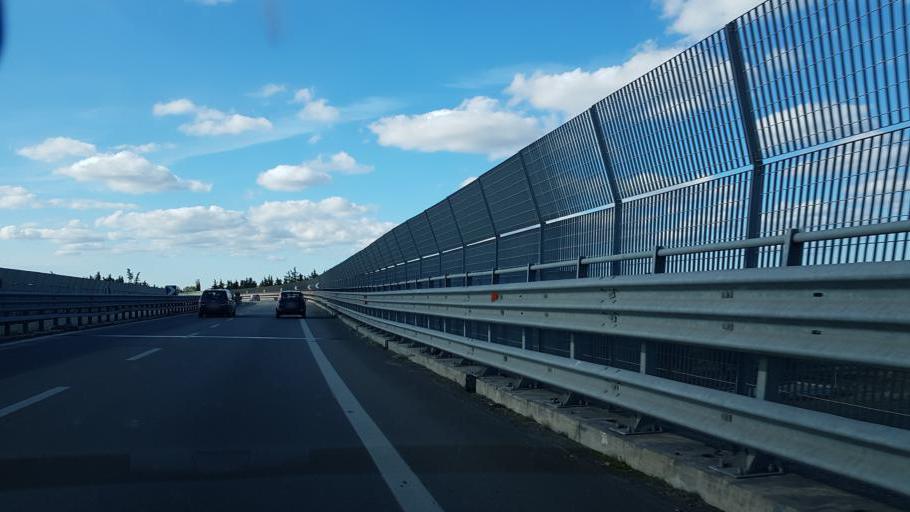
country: IT
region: Apulia
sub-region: Provincia di Lecce
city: Lequile
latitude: 40.3283
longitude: 18.1427
